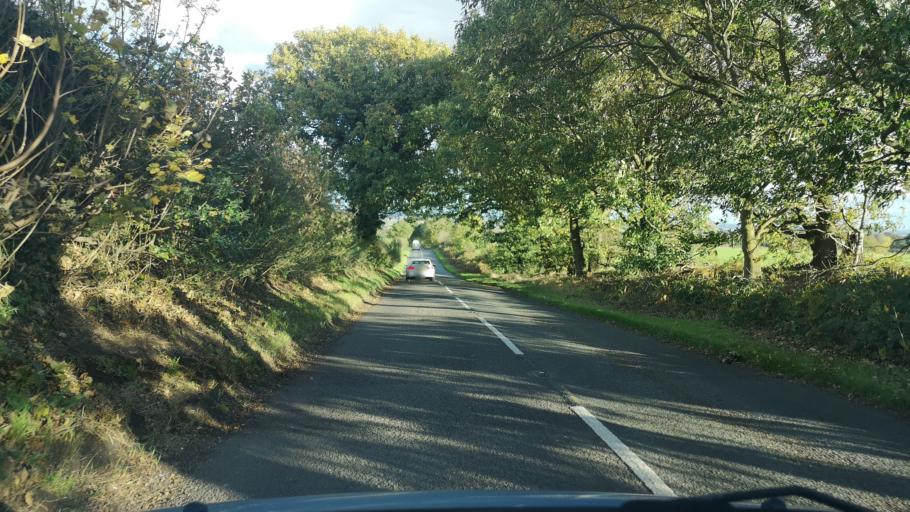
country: GB
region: England
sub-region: City and Borough of Wakefield
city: Woolley
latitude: 53.6208
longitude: -1.5258
